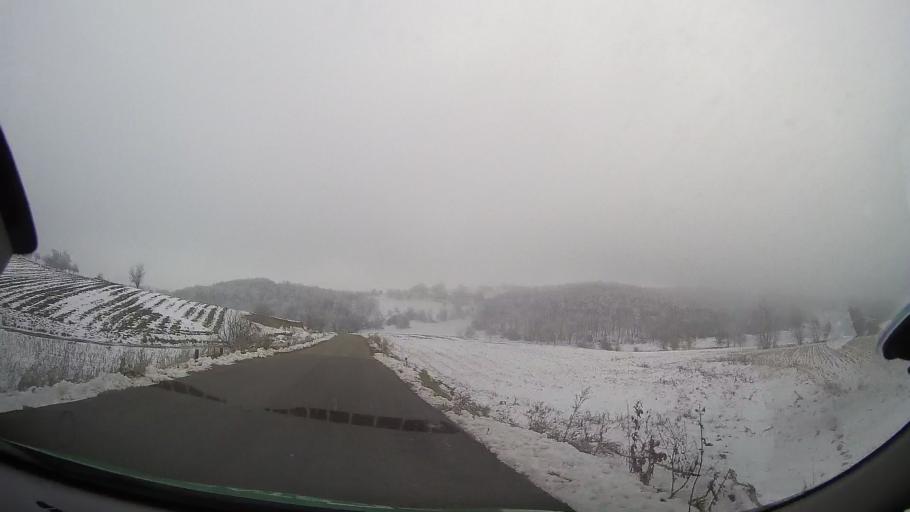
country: RO
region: Bacau
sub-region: Comuna Glavanesti
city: Frumuselu
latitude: 46.2661
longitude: 27.3167
